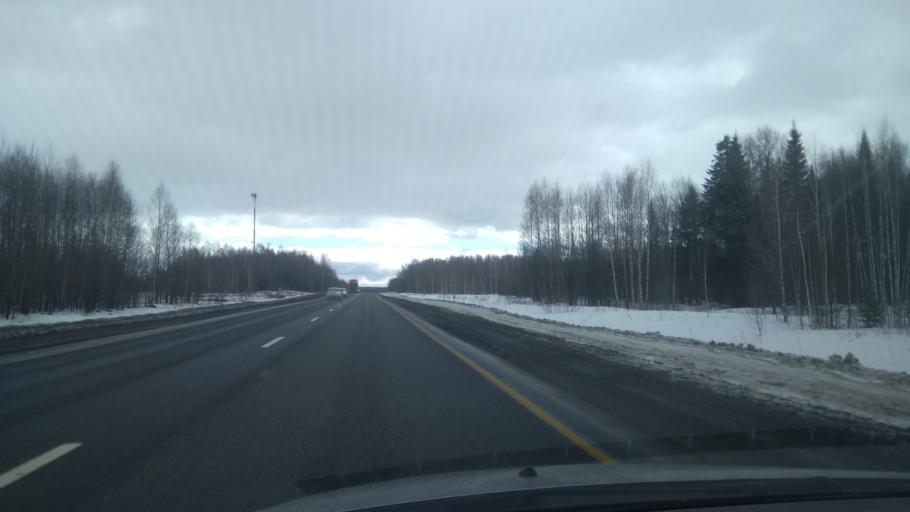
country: RU
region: Perm
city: Orda
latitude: 57.1968
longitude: 57.1118
